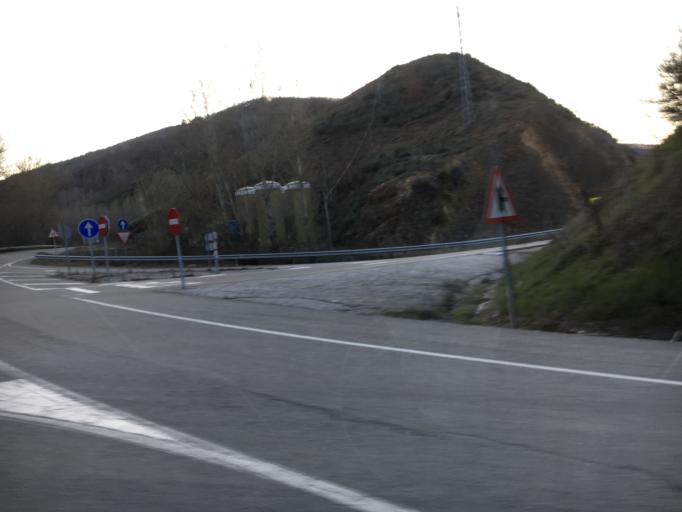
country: ES
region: Castille and Leon
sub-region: Provincia de Leon
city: Trabadelo
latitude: 42.6447
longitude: -6.8761
